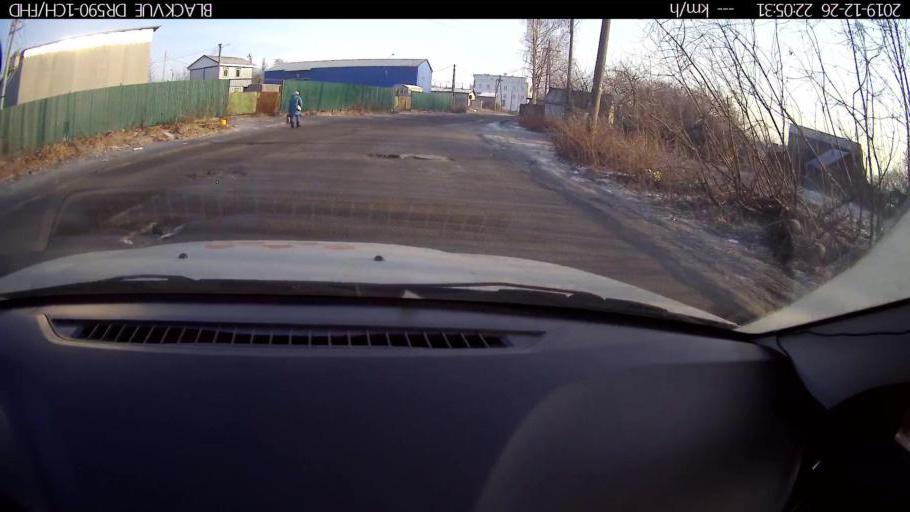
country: RU
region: Nizjnij Novgorod
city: Kstovo
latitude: 56.1459
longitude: 44.2160
